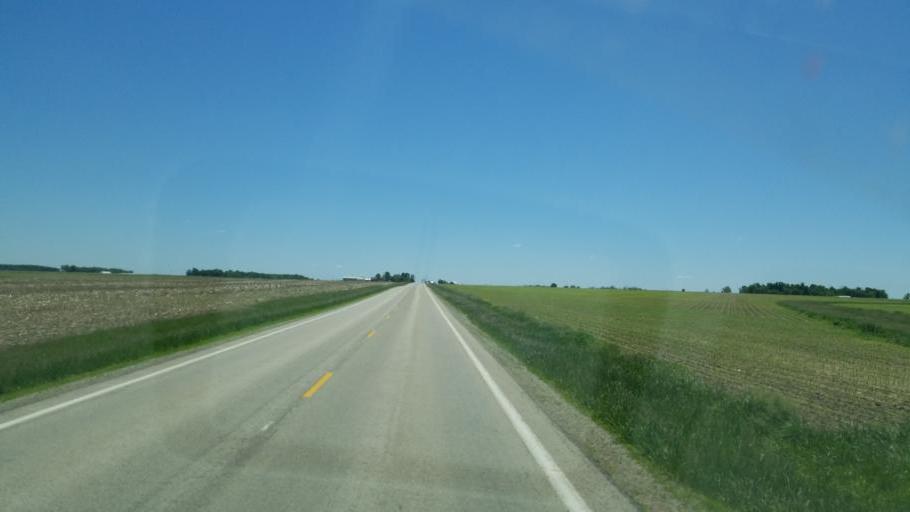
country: US
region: Ohio
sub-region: Darke County
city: Ansonia
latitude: 40.2759
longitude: -84.7069
